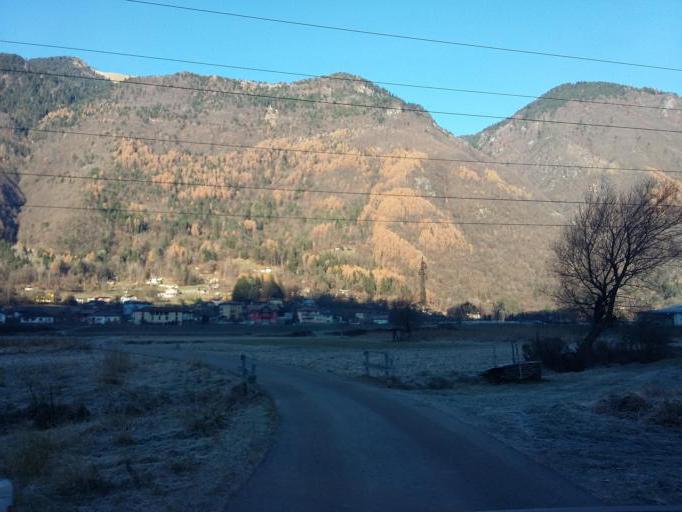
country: IT
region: Trentino-Alto Adige
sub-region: Provincia di Trento
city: Storo
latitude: 45.8520
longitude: 10.5705
